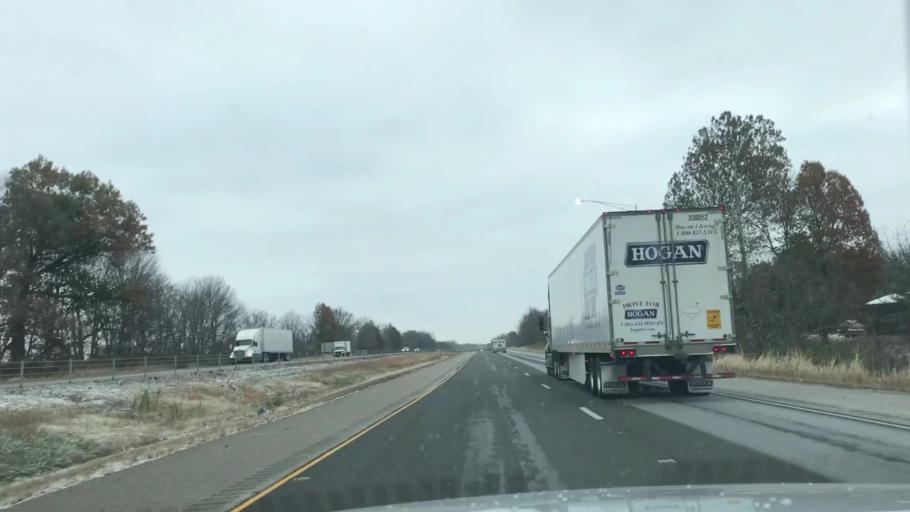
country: US
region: Illinois
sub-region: Madison County
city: Glen Carbon
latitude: 38.7565
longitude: -89.9925
